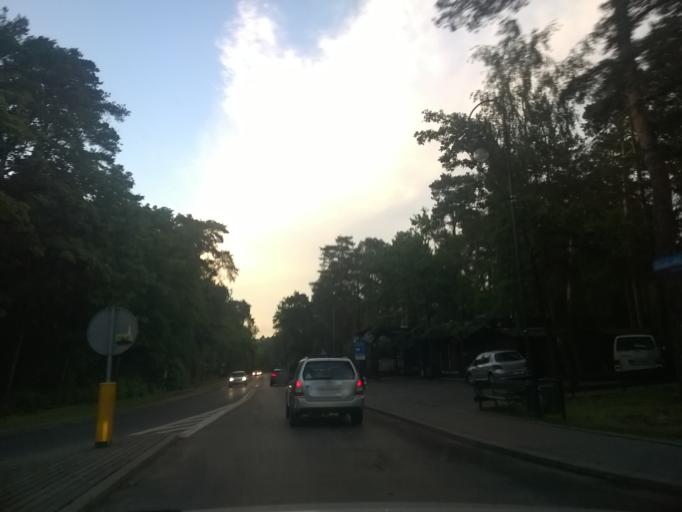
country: PL
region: Masovian Voivodeship
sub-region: Powiat piaseczynski
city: Konstancin-Jeziorna
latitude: 52.0777
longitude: 21.1178
